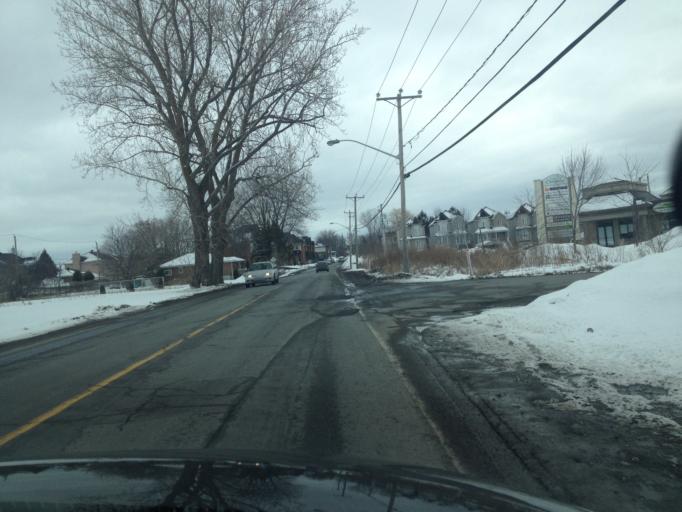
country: CA
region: Quebec
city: Dollard-Des Ormeaux
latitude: 45.5470
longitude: -73.7768
